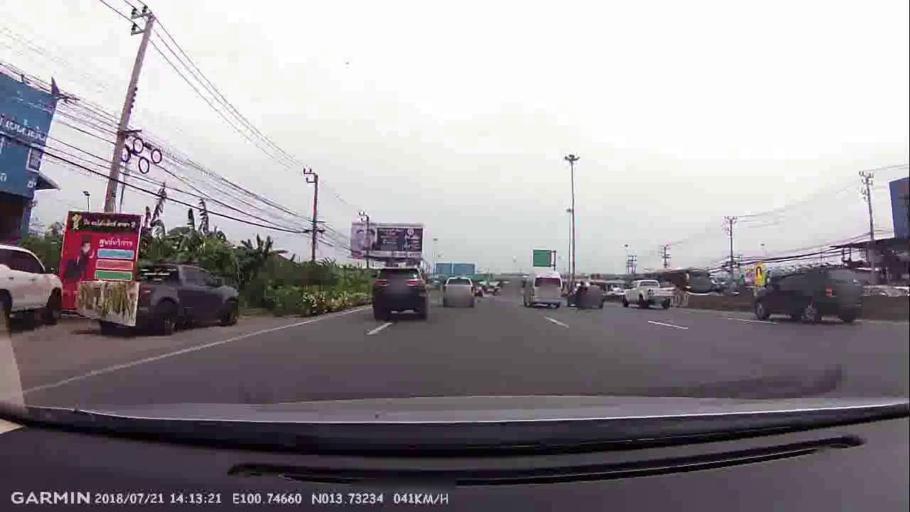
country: TH
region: Bangkok
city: Lat Krabang
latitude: 13.7323
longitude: 100.7466
